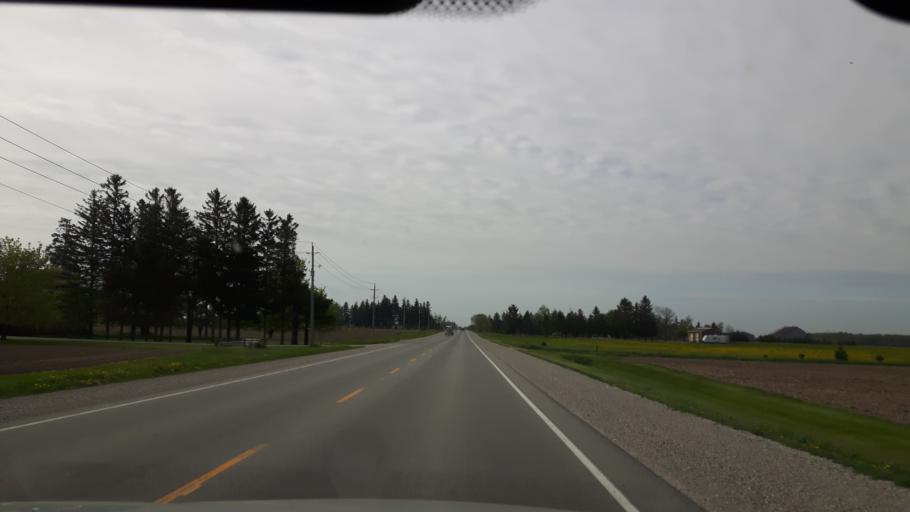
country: CA
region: Ontario
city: South Huron
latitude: 43.3937
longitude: -81.4902
